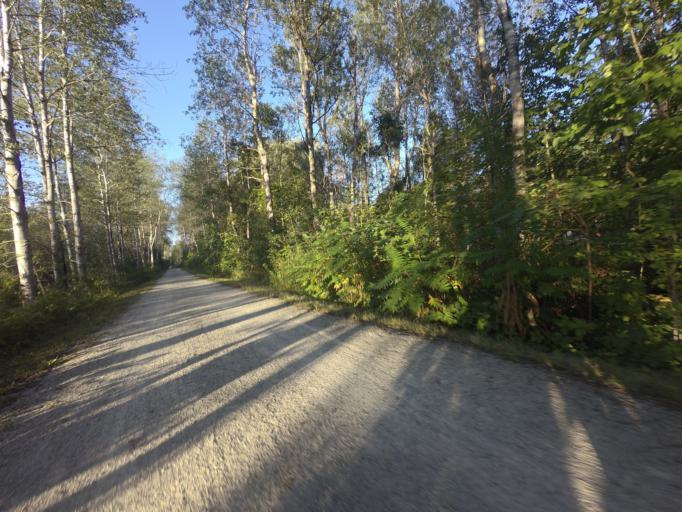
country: CA
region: Ontario
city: Brampton
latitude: 43.8458
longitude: -79.8830
